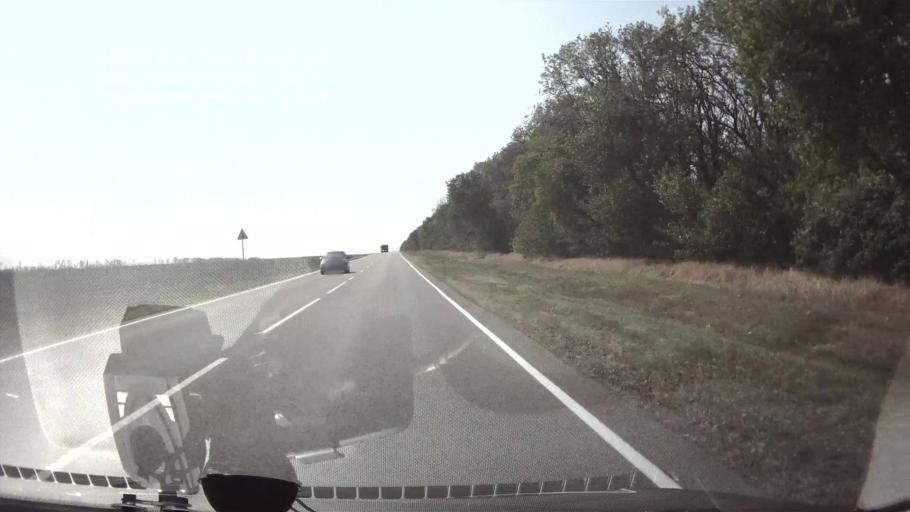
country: RU
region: Krasnodarskiy
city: Dmitriyevskaya
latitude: 45.7977
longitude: 40.7195
